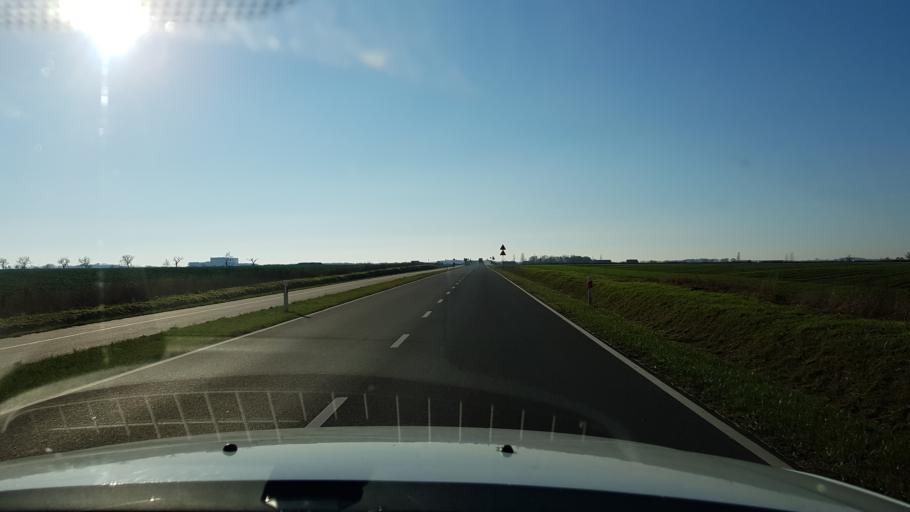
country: PL
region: West Pomeranian Voivodeship
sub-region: Powiat pyrzycki
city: Warnice
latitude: 53.3185
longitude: 14.9857
